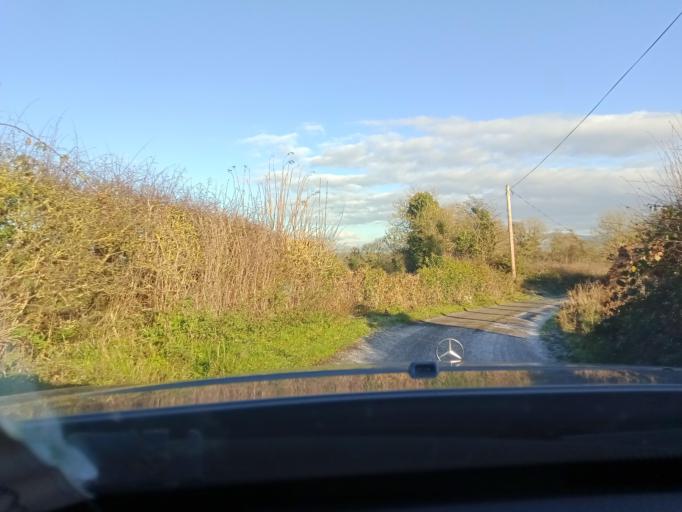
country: IE
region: Leinster
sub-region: Kilkenny
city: Graiguenamanagh
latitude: 52.5643
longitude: -6.9399
